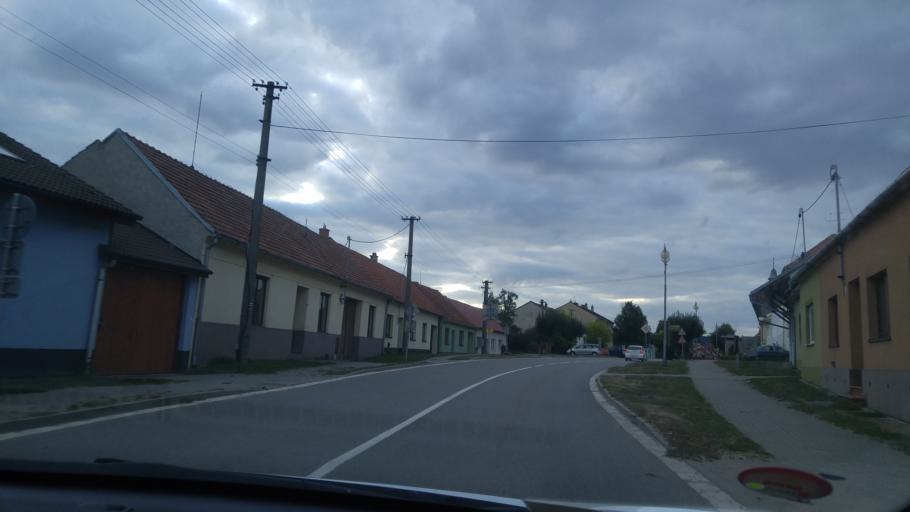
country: CZ
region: South Moravian
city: Ricany
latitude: 49.2101
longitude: 16.4111
